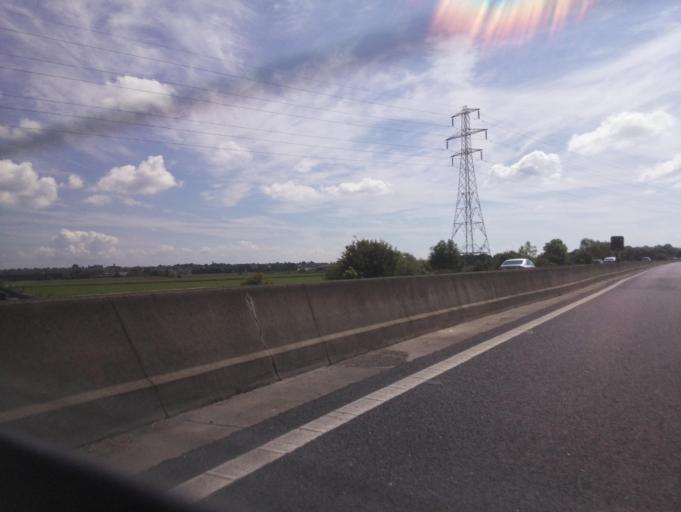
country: GB
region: England
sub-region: North Lincolnshire
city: Gunness
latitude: 53.5527
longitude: -0.6998
